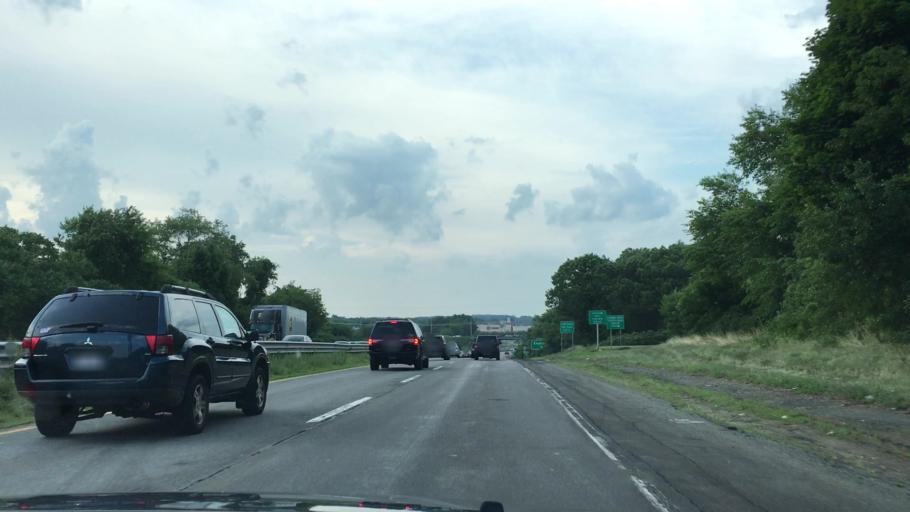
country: US
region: Massachusetts
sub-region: Essex County
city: Peabody
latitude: 42.5444
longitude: -70.9361
